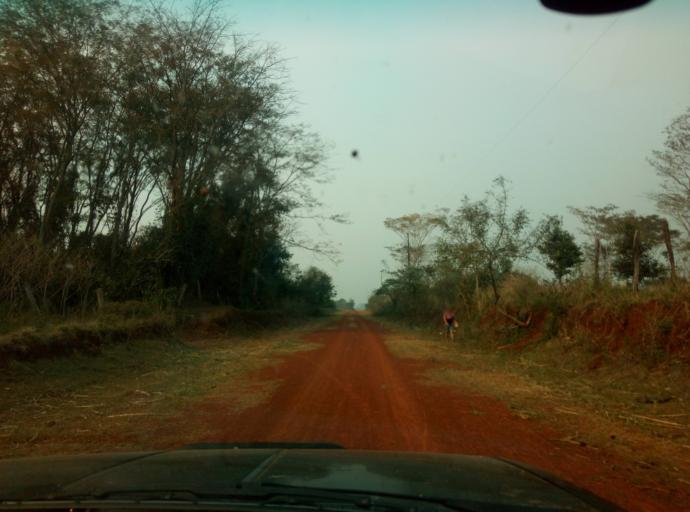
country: PY
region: Caaguazu
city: Carayao
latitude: -25.2052
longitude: -56.2240
